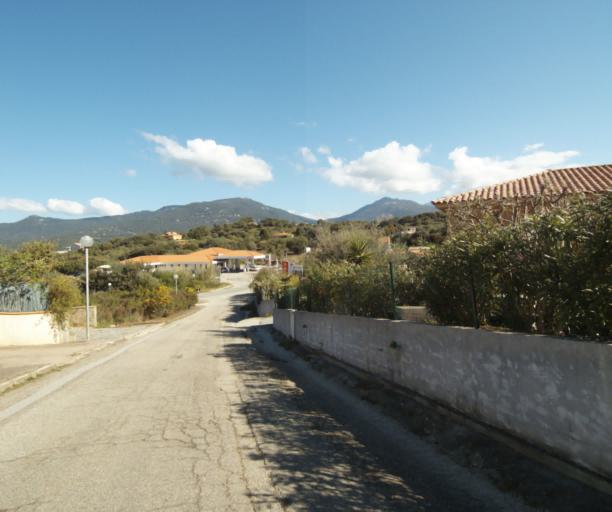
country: FR
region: Corsica
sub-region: Departement de la Corse-du-Sud
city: Propriano
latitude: 41.6707
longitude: 8.9091
